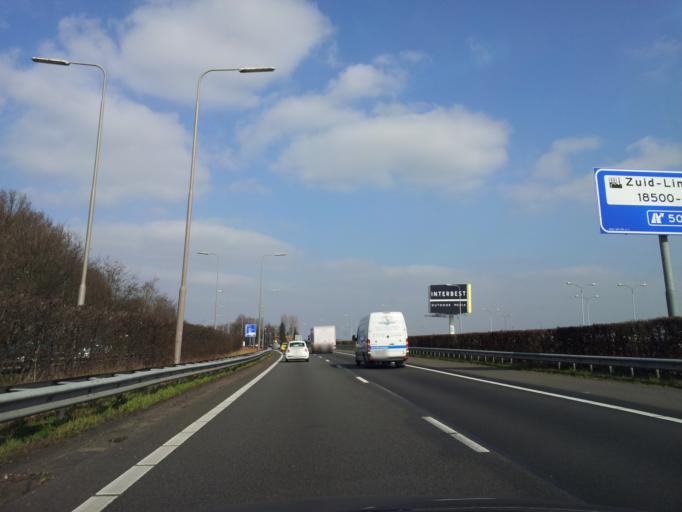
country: NL
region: Limburg
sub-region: Gemeente Stein
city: Elsloo
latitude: 50.9164
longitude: 5.7690
